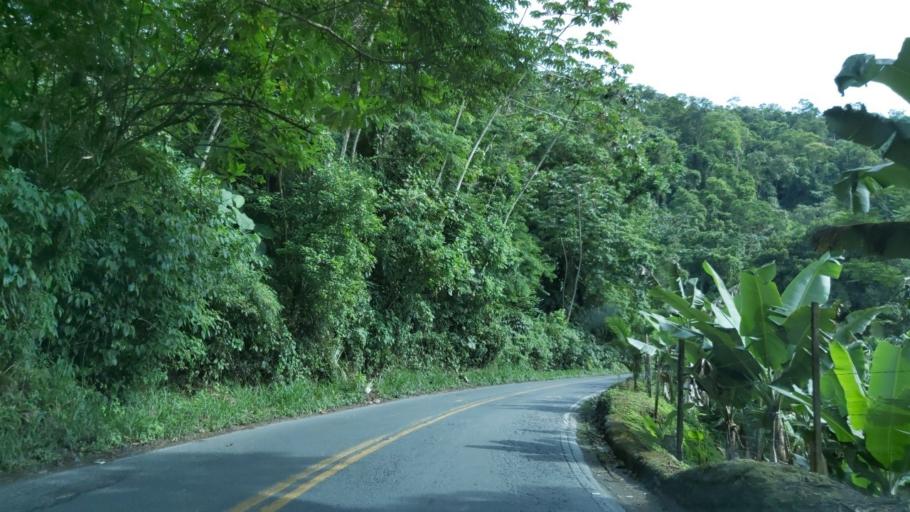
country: BR
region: Sao Paulo
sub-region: Juquia
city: Juquia
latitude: -24.0861
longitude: -47.6125
